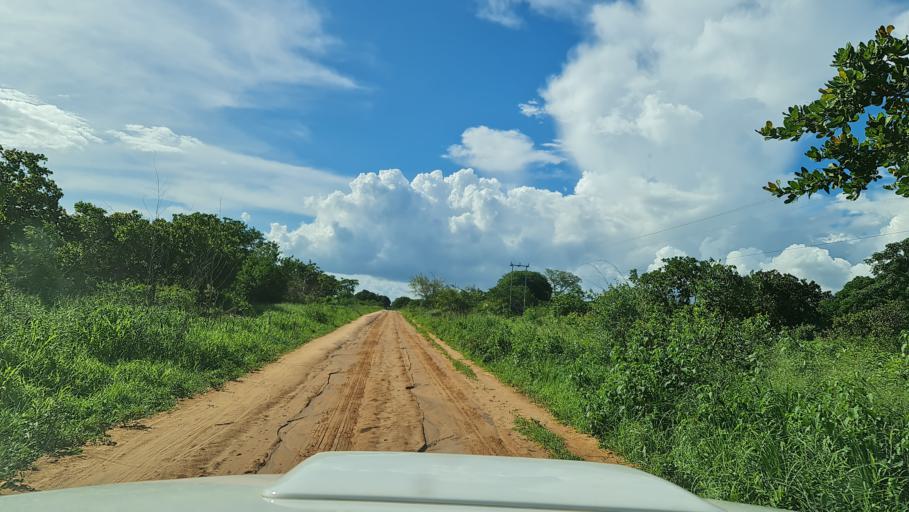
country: MZ
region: Nampula
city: Ilha de Mocambique
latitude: -15.2965
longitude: 40.1232
